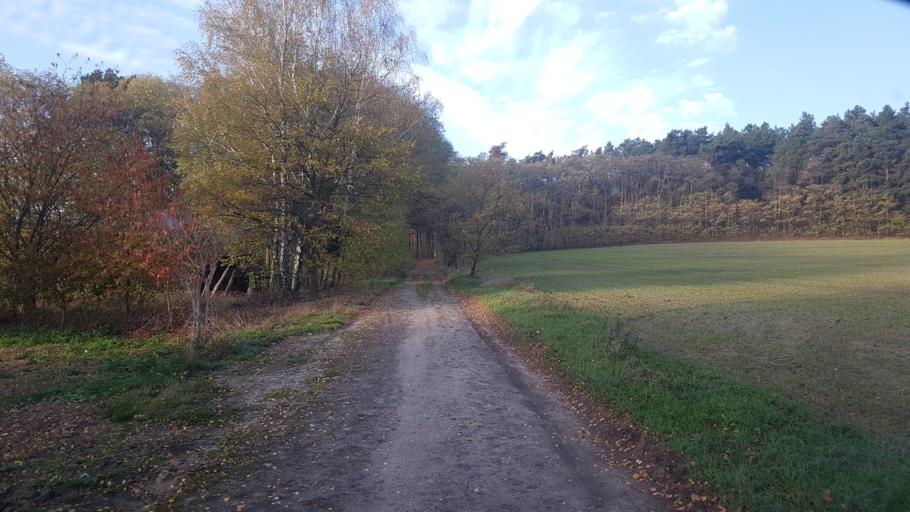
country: DE
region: Brandenburg
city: Calau
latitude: 51.6924
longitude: 13.9653
